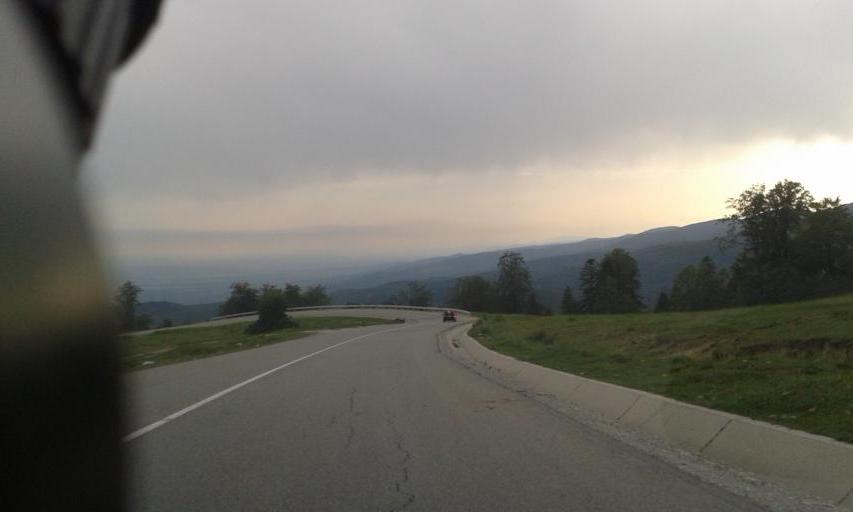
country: RO
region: Gorj
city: Novaci-Straini
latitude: 45.2342
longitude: 23.6898
